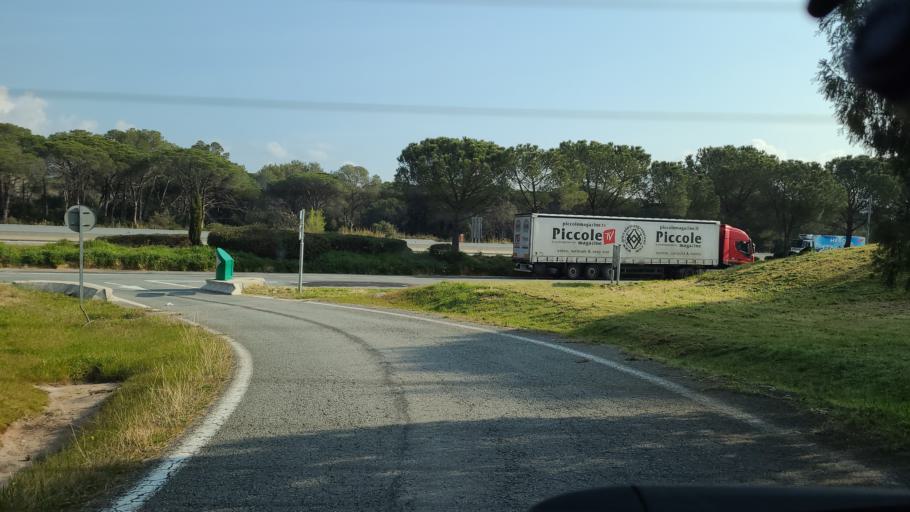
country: FR
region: Provence-Alpes-Cote d'Azur
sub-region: Departement du Var
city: Puget-sur-Argens
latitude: 43.4644
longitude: 6.6755
